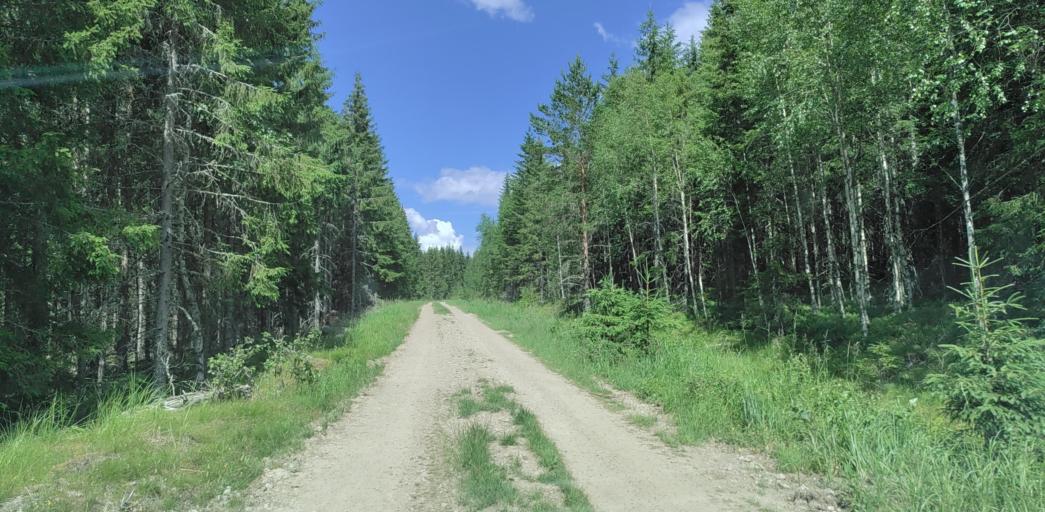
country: SE
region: Vaermland
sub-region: Hagfors Kommun
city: Ekshaerad
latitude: 60.0633
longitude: 13.3391
